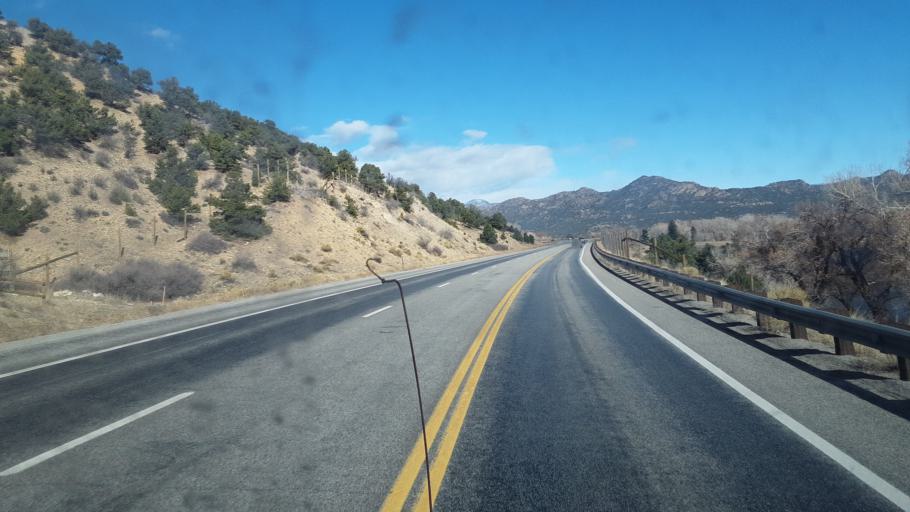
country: US
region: Colorado
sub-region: Chaffee County
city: Buena Vista
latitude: 38.7856
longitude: -106.1142
